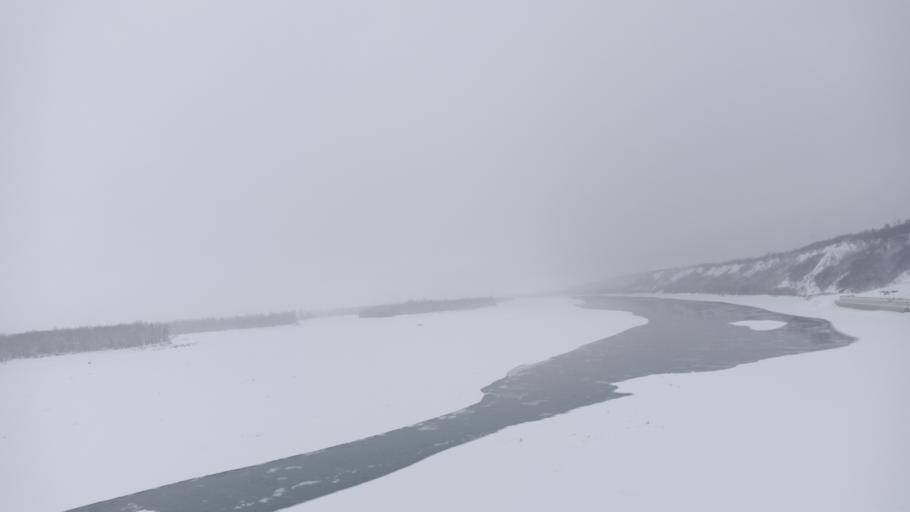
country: RU
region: Altai Krai
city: Zaton
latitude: 53.3238
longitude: 83.8020
